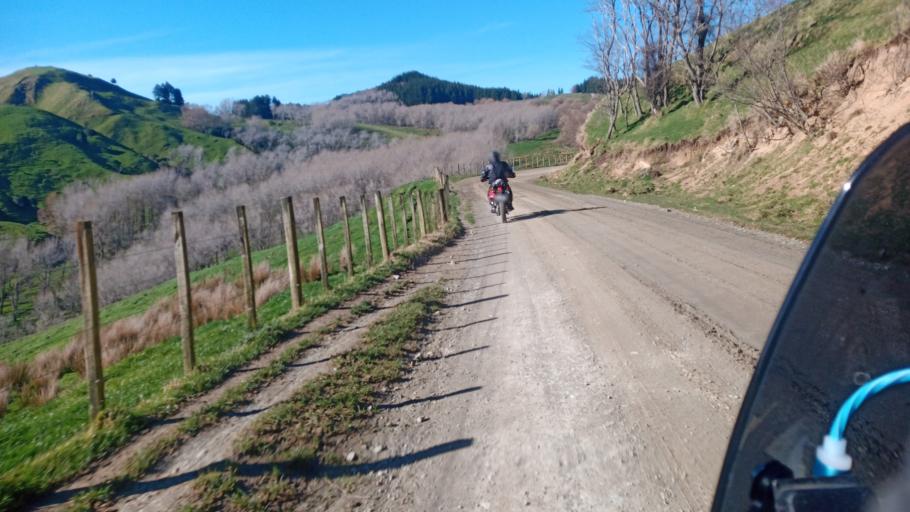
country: NZ
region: Gisborne
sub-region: Gisborne District
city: Gisborne
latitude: -38.2953
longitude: 177.9000
